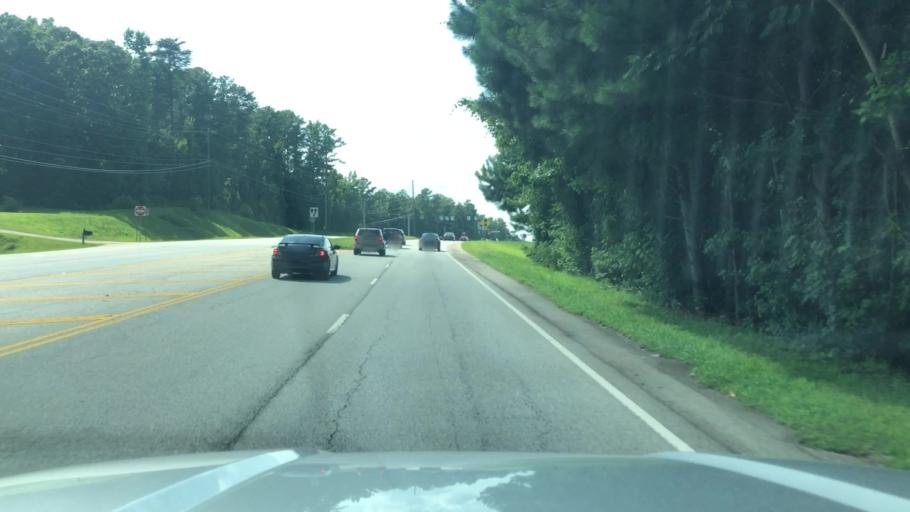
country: US
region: Georgia
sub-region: Douglas County
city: Lithia Springs
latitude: 33.7024
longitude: -84.6558
